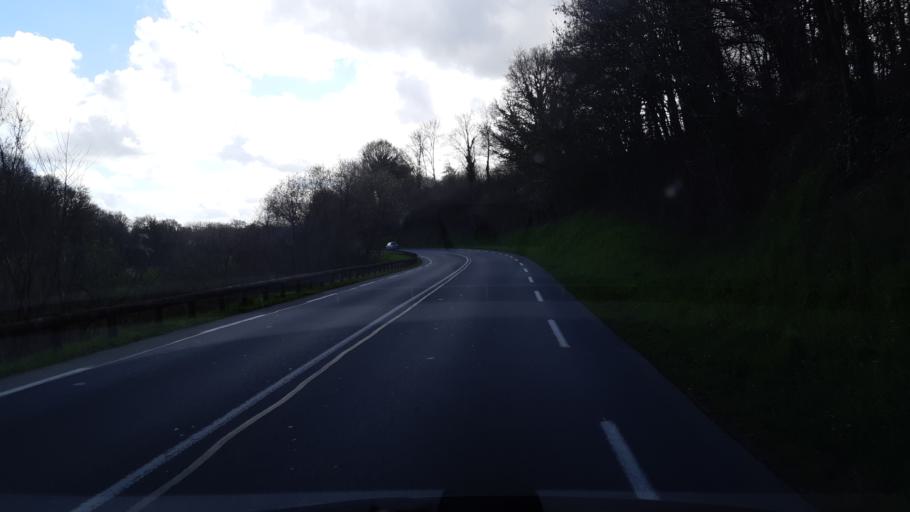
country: FR
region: Lower Normandy
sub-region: Departement de la Manche
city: Agneaux
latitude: 49.0755
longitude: -1.1265
